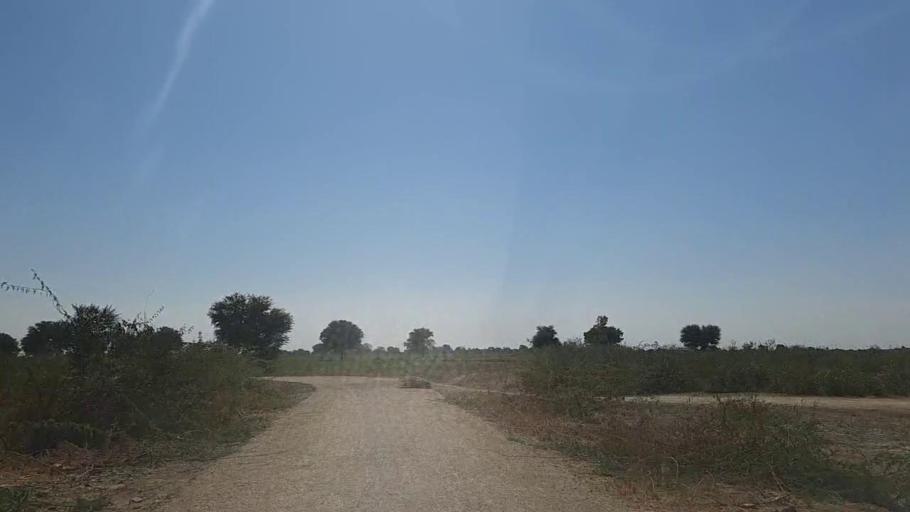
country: PK
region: Sindh
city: Dhoro Naro
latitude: 25.3530
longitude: 69.5340
